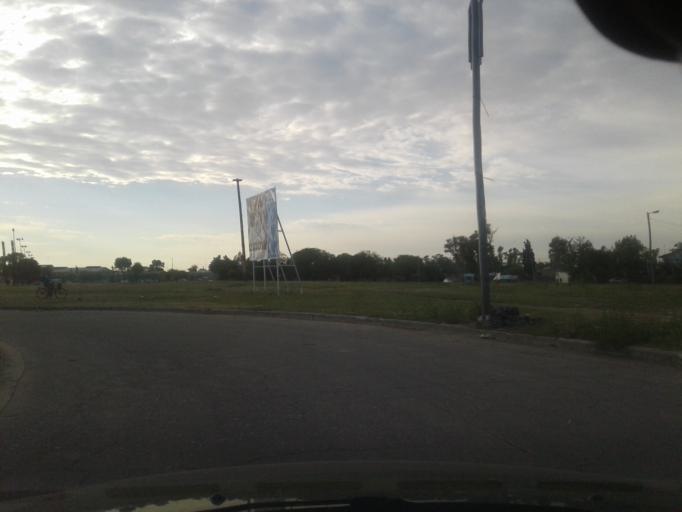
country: AR
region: Santa Fe
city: Granadero Baigorria
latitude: -32.8906
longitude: -60.7249
